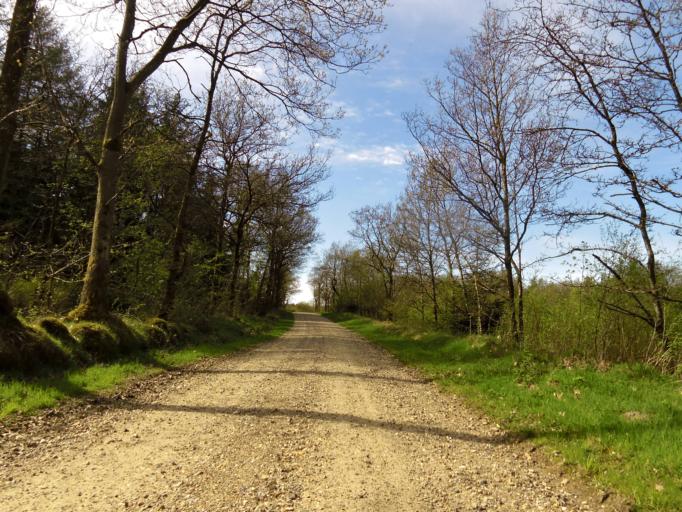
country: DK
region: Central Jutland
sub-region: Holstebro Kommune
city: Vinderup
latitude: 56.4764
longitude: 8.8757
